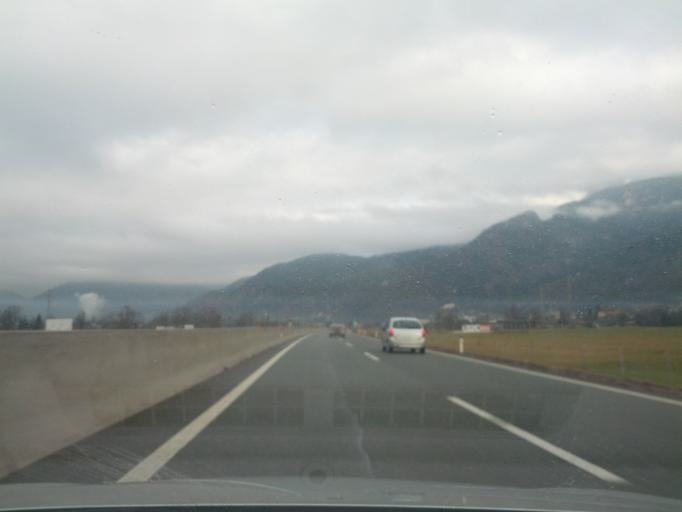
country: SI
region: Zirovnica
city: Zirovnica
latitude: 46.3940
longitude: 14.1343
